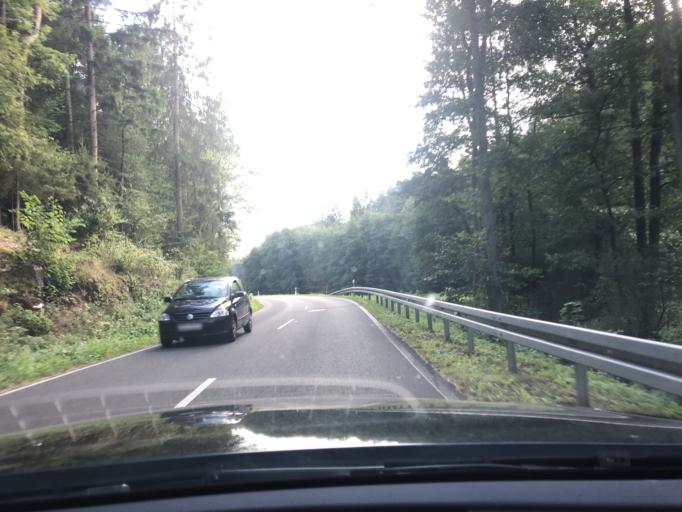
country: DE
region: Bavaria
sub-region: Regierungsbezirk Unterfranken
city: Breitbrunn
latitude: 50.0172
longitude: 10.6780
